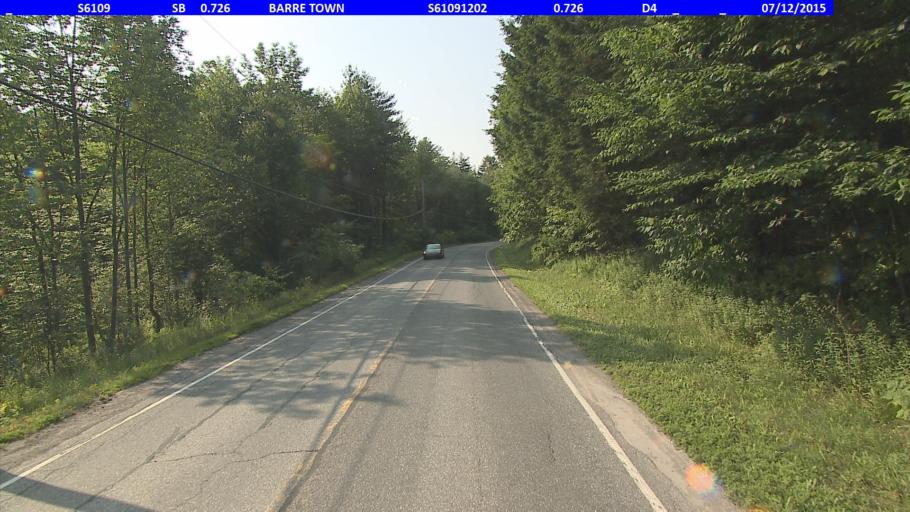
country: US
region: Vermont
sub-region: Washington County
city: South Barre
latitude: 44.1649
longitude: -72.4921
